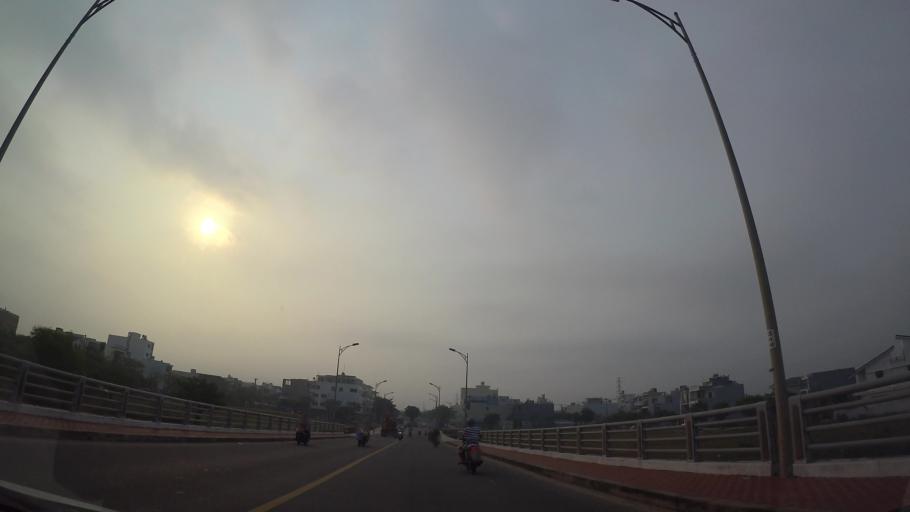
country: VN
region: Da Nang
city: Cam Le
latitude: 16.0236
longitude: 108.2238
